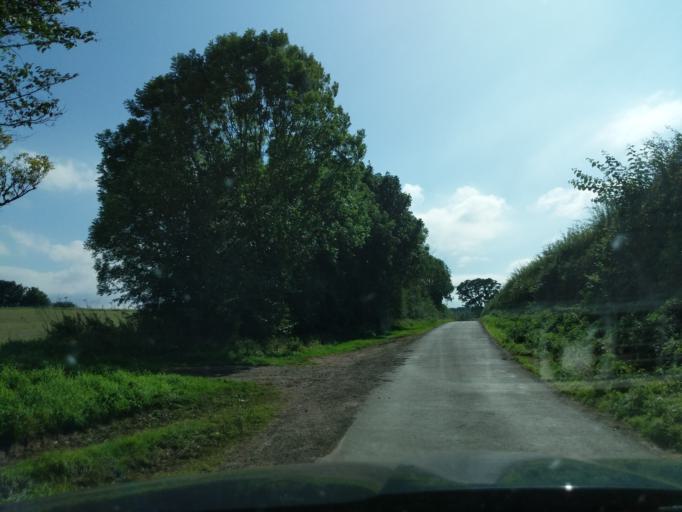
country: GB
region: England
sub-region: Northumberland
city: Ford
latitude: 55.6395
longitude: -2.1372
